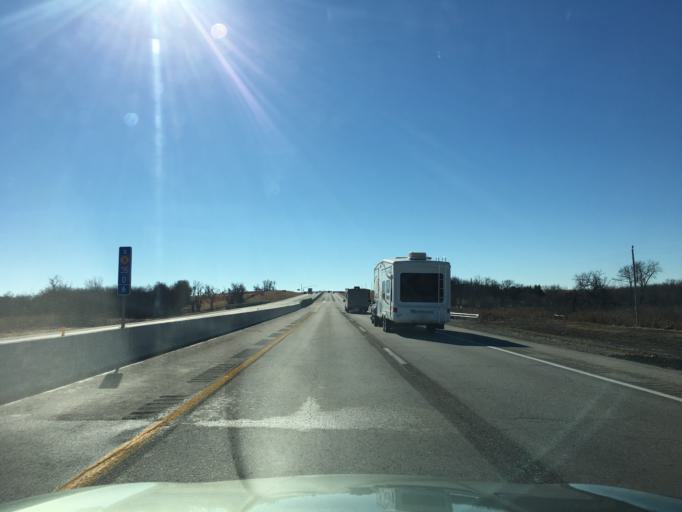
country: US
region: Oklahoma
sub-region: Kay County
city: Blackwell
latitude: 37.0078
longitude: -97.3400
